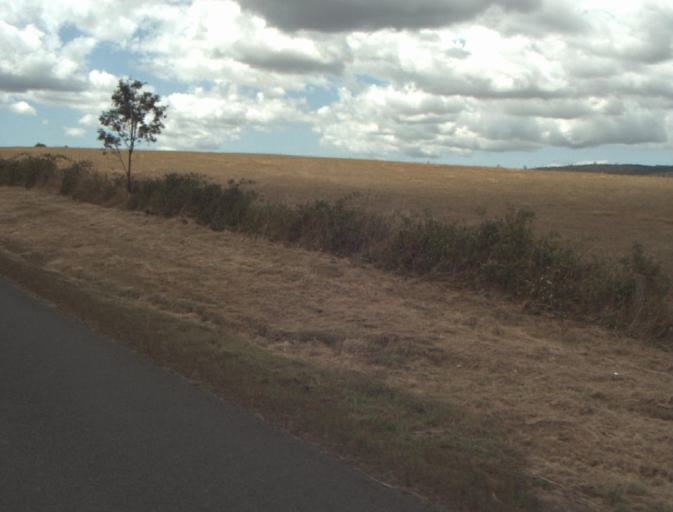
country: AU
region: Tasmania
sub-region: Launceston
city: Mayfield
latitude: -41.2170
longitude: 147.1215
